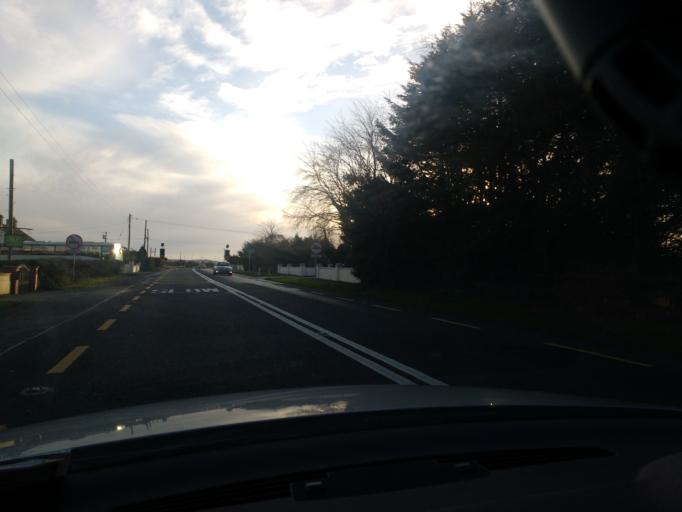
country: IE
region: Munster
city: Thurles
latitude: 52.6343
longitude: -7.7789
